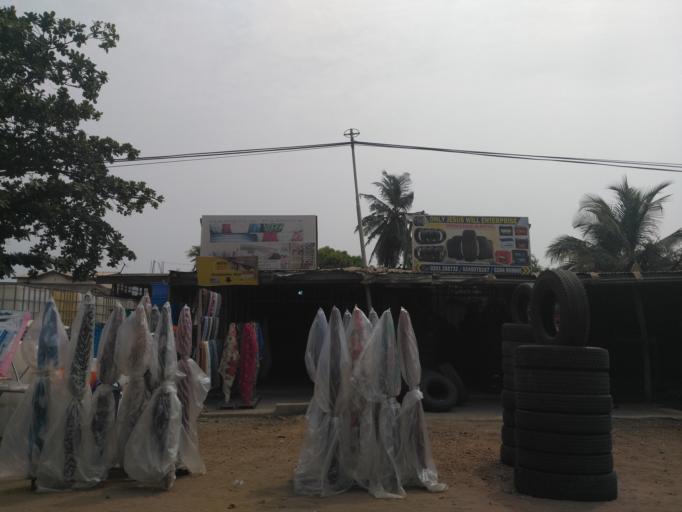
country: GH
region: Greater Accra
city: Nungua
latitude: 5.5992
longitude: -0.0808
